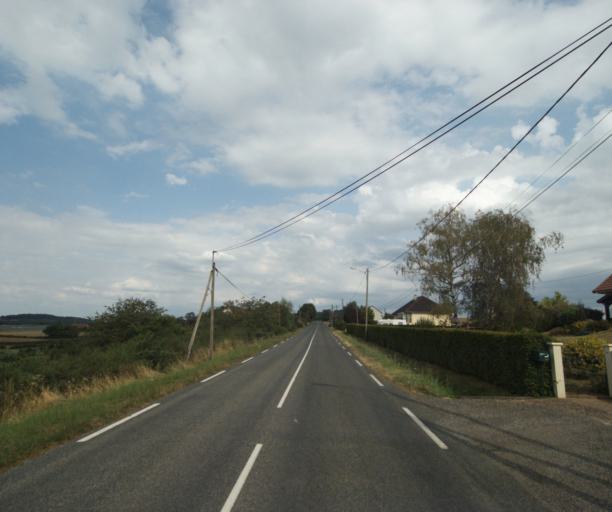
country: FR
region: Bourgogne
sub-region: Departement de Saone-et-Loire
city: Gueugnon
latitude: 46.6015
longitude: 4.0932
